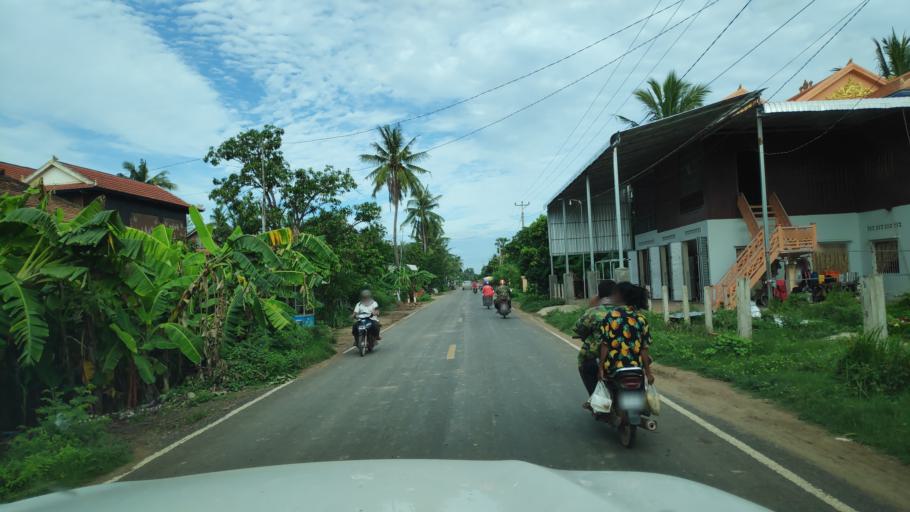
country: KH
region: Kampong Cham
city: Kampong Cham
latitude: 11.9465
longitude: 105.2527
